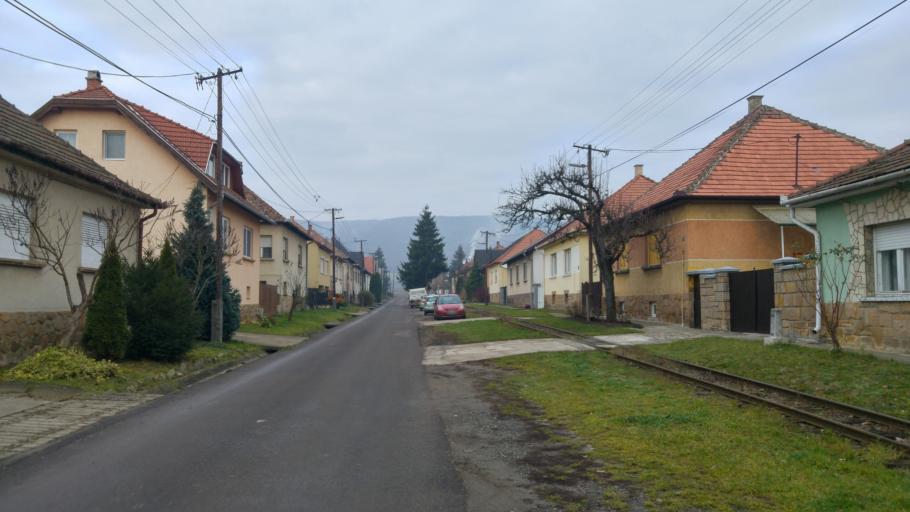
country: HU
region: Pest
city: Kismaros
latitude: 47.8670
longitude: 18.9995
